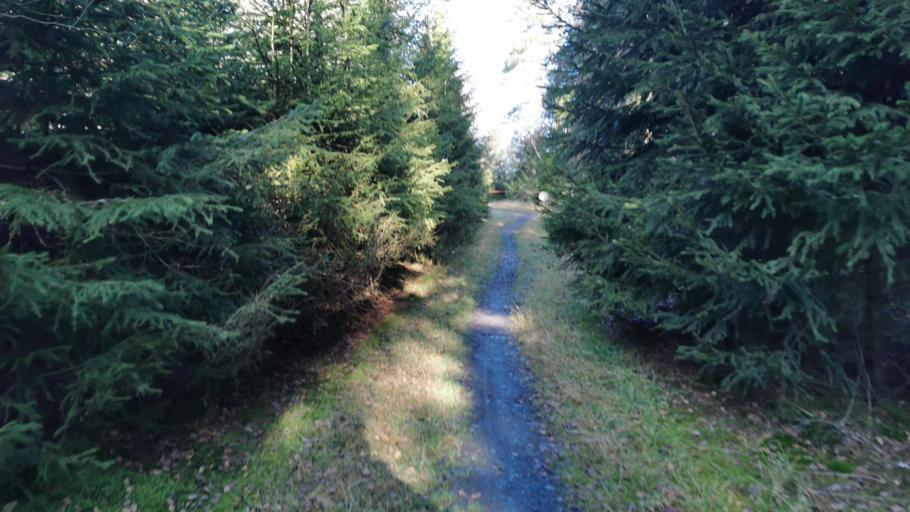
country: DE
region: Bavaria
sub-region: Upper Franconia
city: Reichenbach
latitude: 50.4593
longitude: 11.4395
